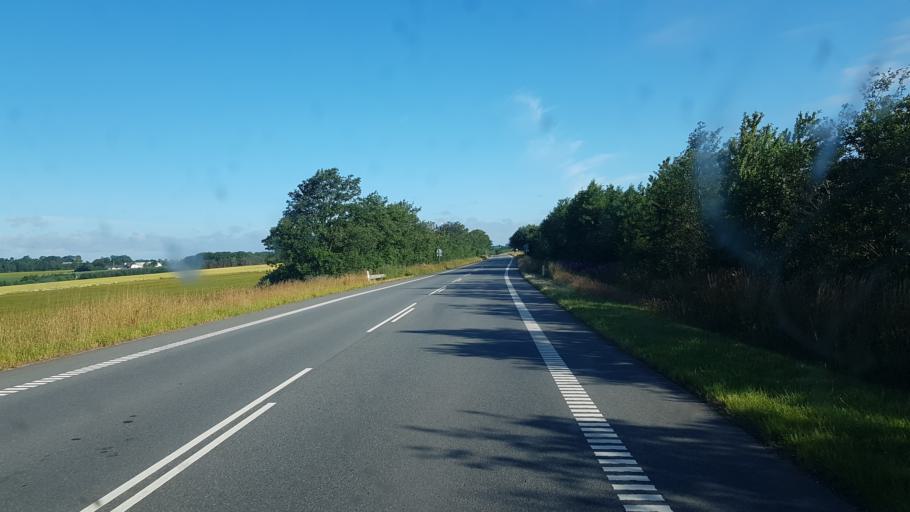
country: DK
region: South Denmark
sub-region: Vejen Kommune
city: Rodding
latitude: 55.3807
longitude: 9.0535
